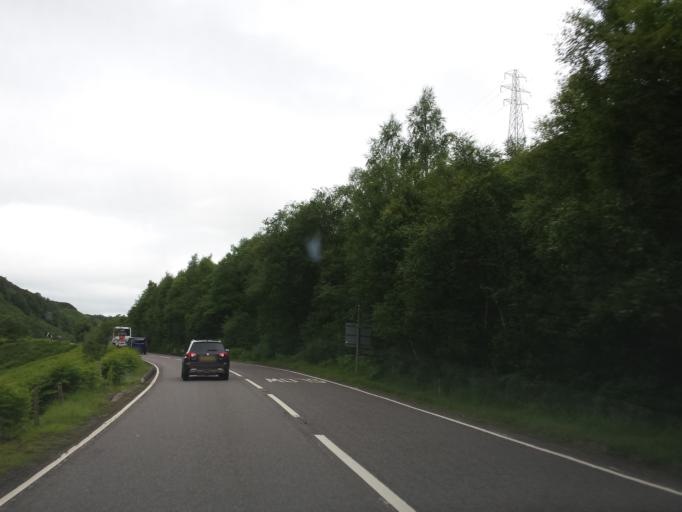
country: GB
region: Scotland
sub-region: Stirling
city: Callander
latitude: 56.4107
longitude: -4.3146
